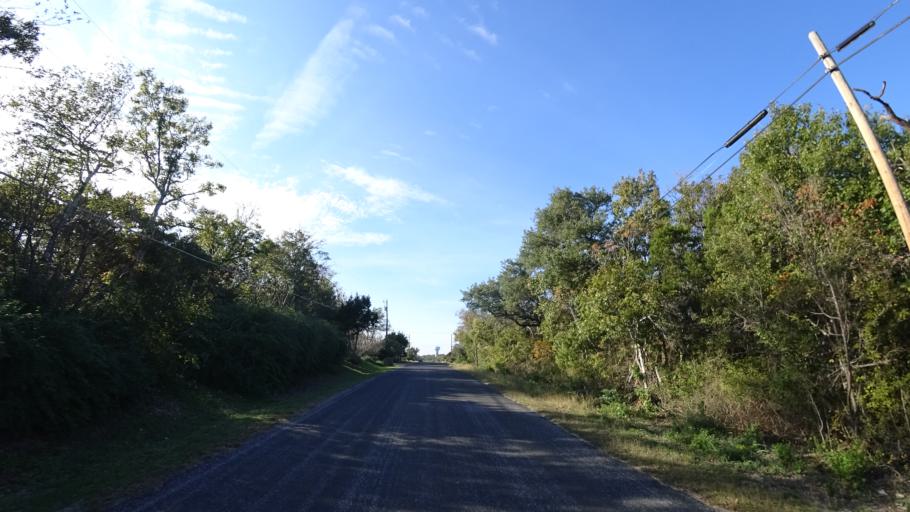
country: US
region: Texas
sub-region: Travis County
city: Barton Creek
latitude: 30.2384
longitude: -97.9134
